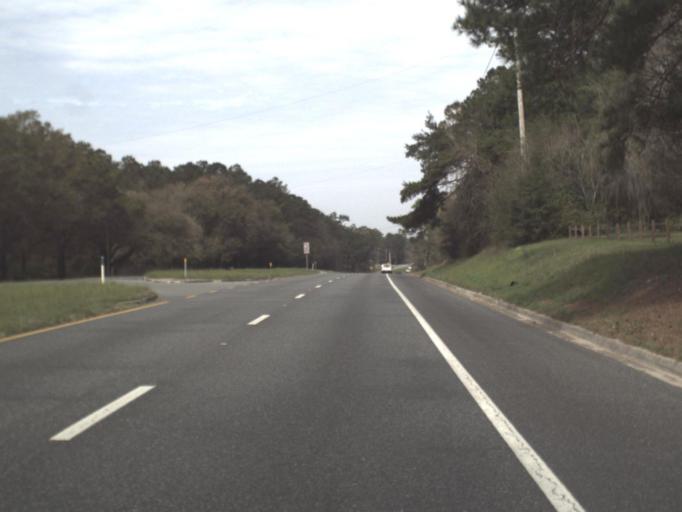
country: US
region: Florida
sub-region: Gadsden County
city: Midway
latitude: 30.4650
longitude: -84.3959
